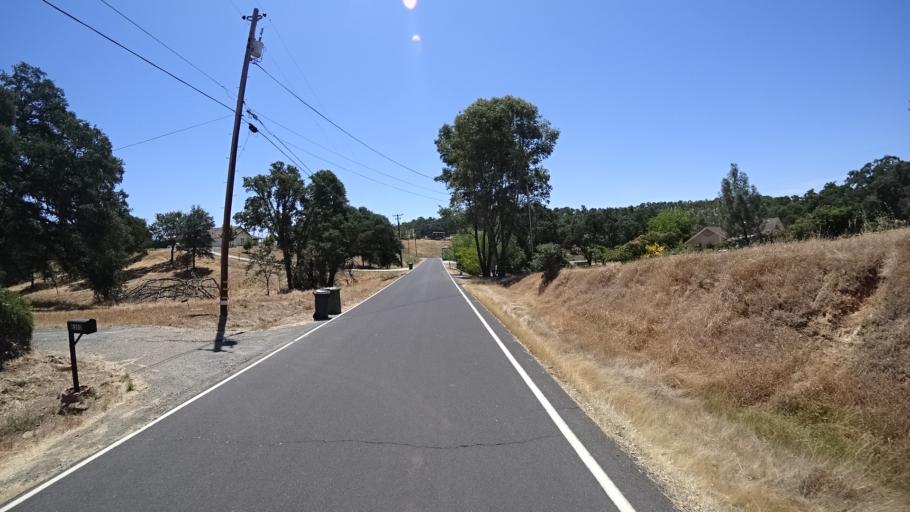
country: US
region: California
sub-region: Calaveras County
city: Rancho Calaveras
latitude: 38.1258
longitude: -120.8691
